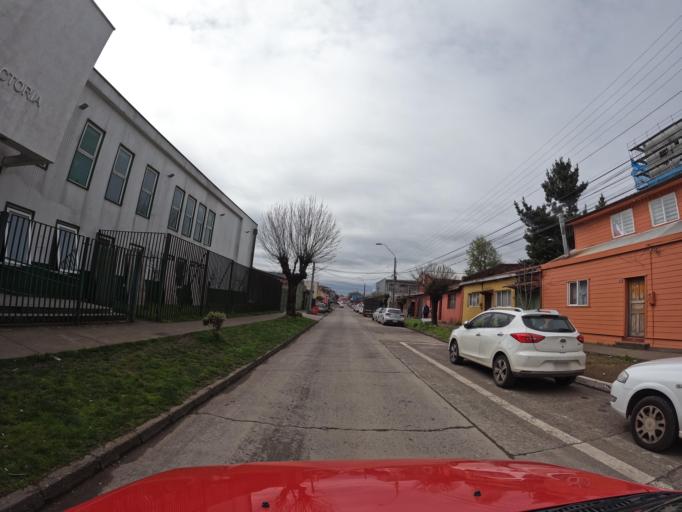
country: CL
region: Araucania
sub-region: Provincia de Malleco
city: Victoria
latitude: -38.2367
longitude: -72.3359
